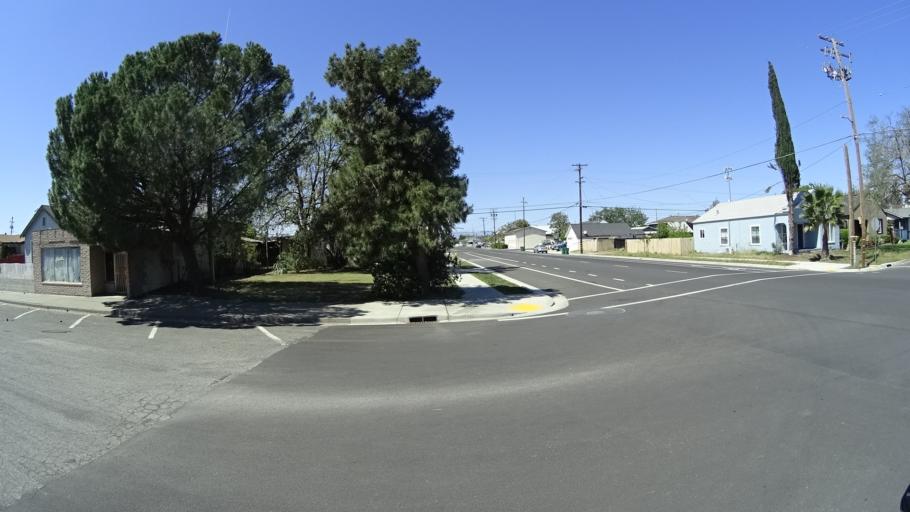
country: US
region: California
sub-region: Glenn County
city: Orland
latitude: 39.7495
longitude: -122.1941
